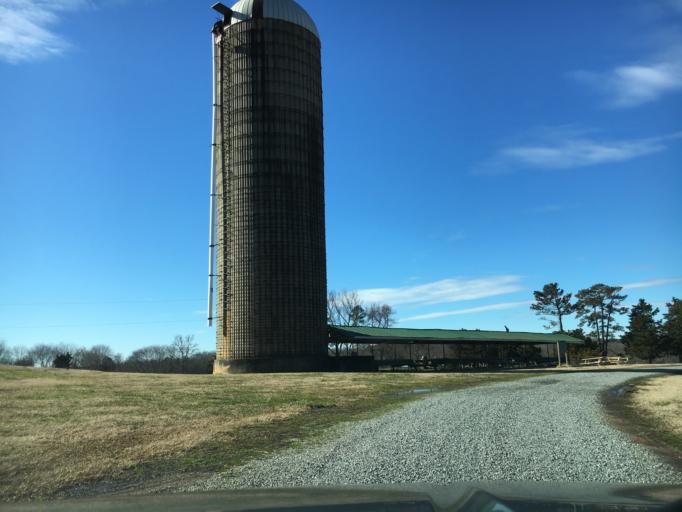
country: US
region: Virginia
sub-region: Halifax County
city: South Boston
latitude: 36.7179
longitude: -78.8675
